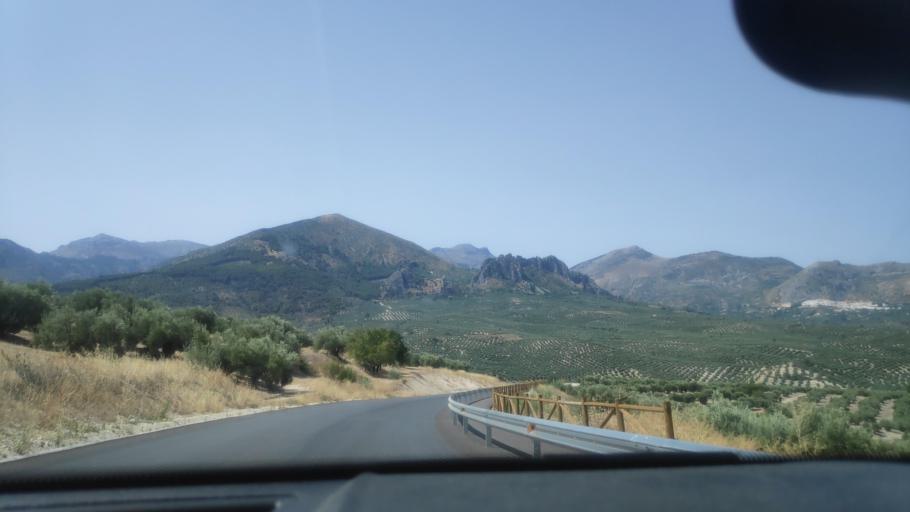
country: ES
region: Andalusia
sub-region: Provincia de Jaen
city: Jodar
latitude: 37.8110
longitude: -3.4129
